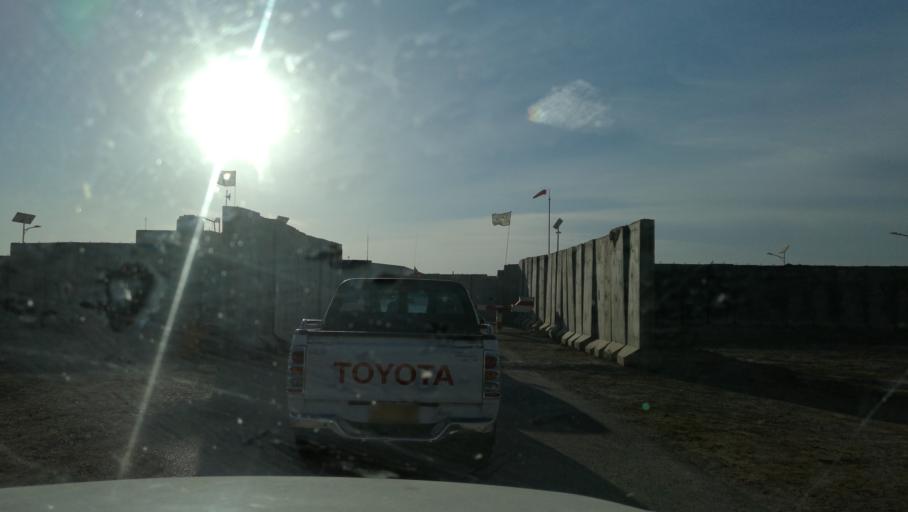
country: IQ
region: Dhi Qar
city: Ar Rifa`i
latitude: 31.7941
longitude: 46.0640
